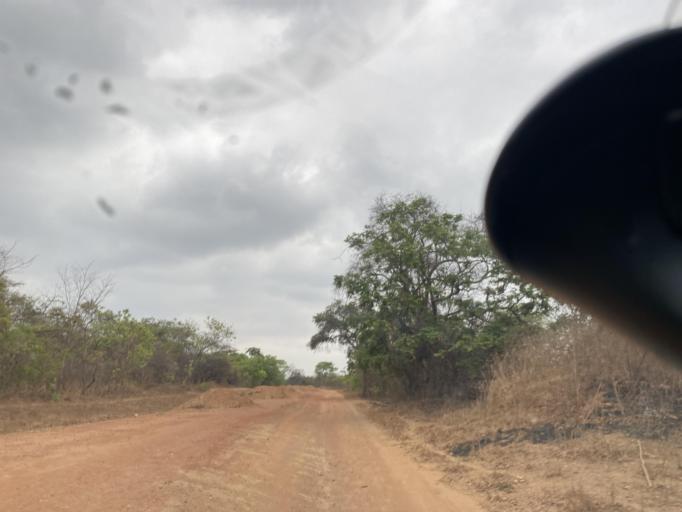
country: ZM
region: Lusaka
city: Chongwe
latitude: -15.2256
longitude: 28.7376
